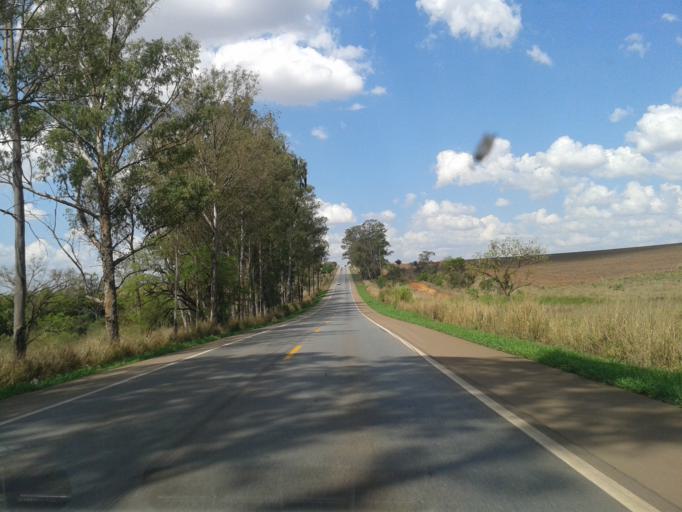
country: BR
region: Minas Gerais
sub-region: Luz
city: Luz
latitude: -19.7842
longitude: -45.7051
